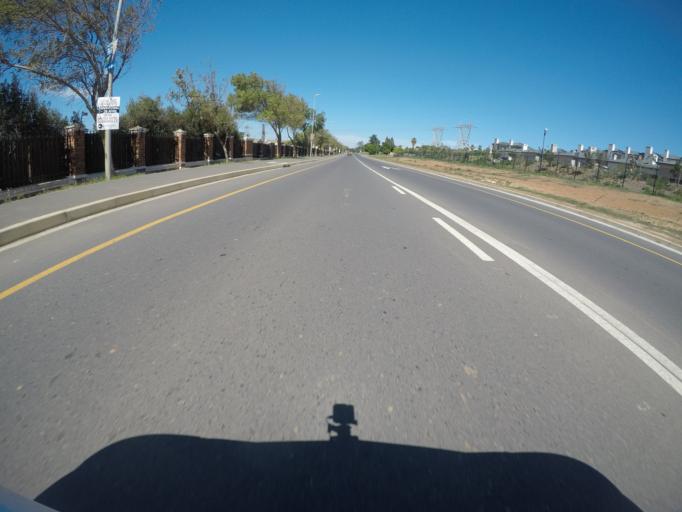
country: ZA
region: Western Cape
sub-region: City of Cape Town
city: Kraaifontein
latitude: -33.8209
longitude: 18.6357
